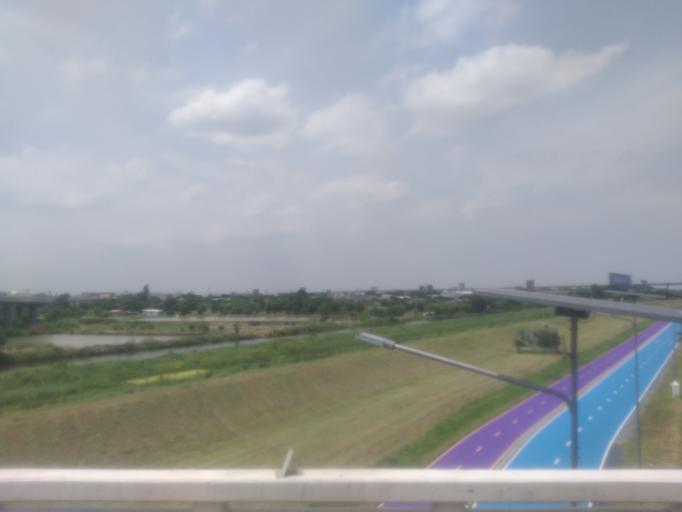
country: TH
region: Bangkok
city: Lat Krabang
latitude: 13.7158
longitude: 100.7471
